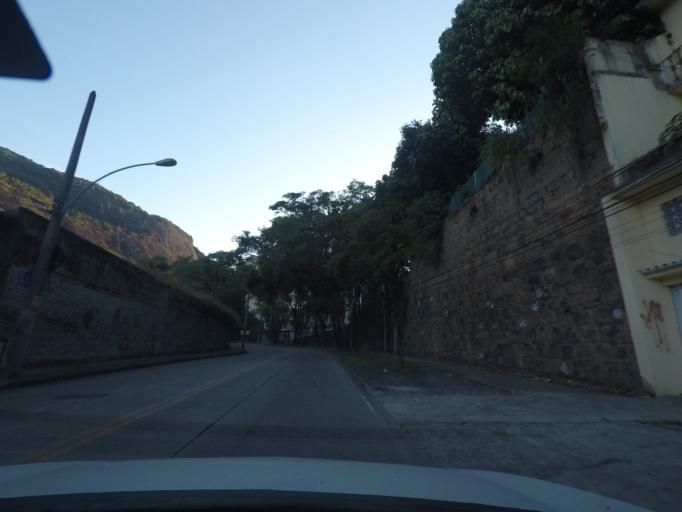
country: BR
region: Rio de Janeiro
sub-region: Rio De Janeiro
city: Rio de Janeiro
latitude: -22.9463
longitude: -43.2590
